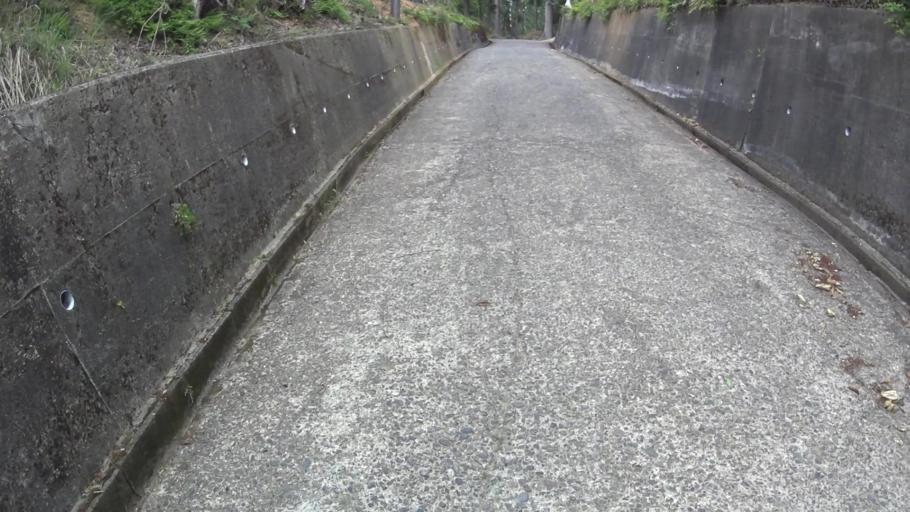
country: JP
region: Nara
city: Yoshino-cho
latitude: 34.3441
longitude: 135.8811
